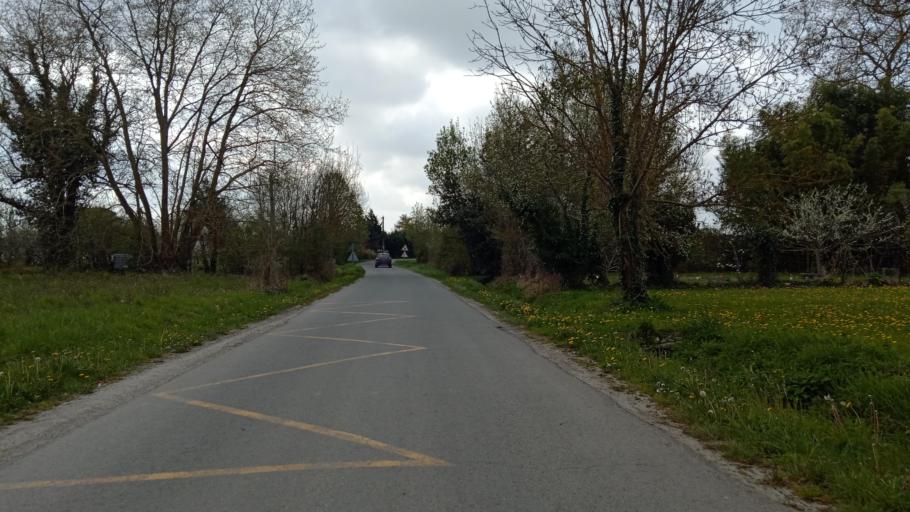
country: FR
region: Poitou-Charentes
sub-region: Departement de la Charente-Maritime
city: Verines
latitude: 46.1534
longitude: -0.9327
